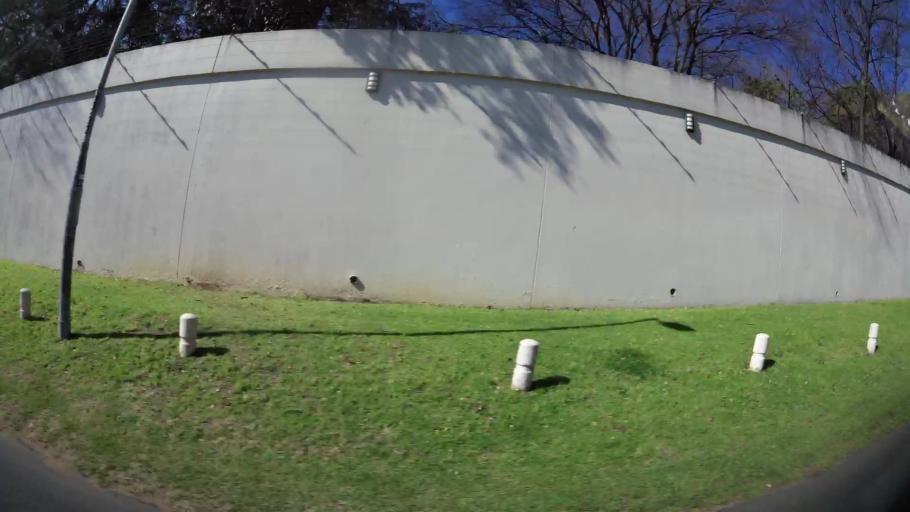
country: ZA
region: Gauteng
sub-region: City of Johannesburg Metropolitan Municipality
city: Johannesburg
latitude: -26.1108
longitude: 28.0355
